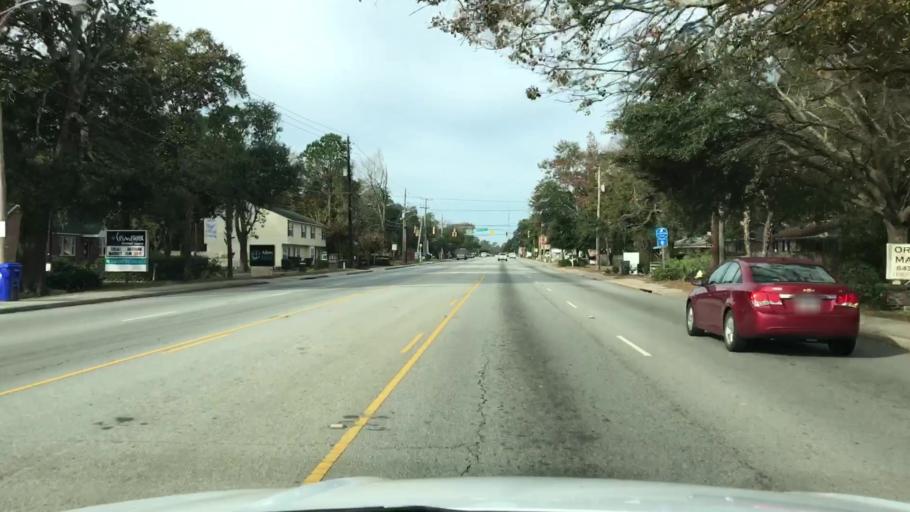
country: US
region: South Carolina
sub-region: Charleston County
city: North Charleston
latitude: 32.7984
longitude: -80.0046
